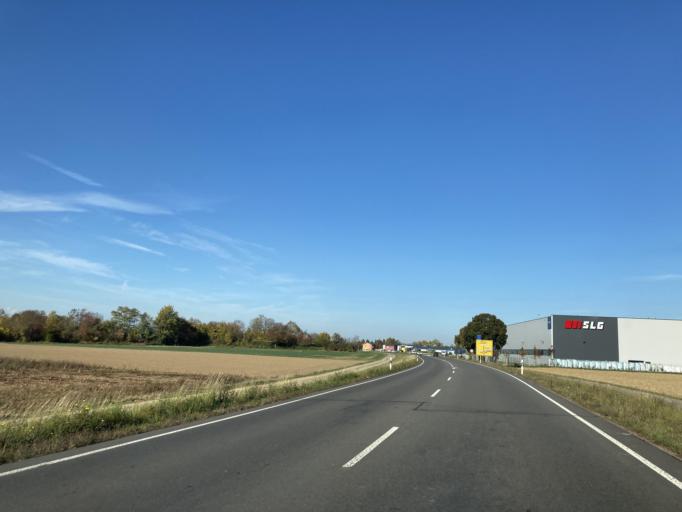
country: DE
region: Baden-Wuerttemberg
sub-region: Freiburg Region
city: Buggingen
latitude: 47.8450
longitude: 7.6249
